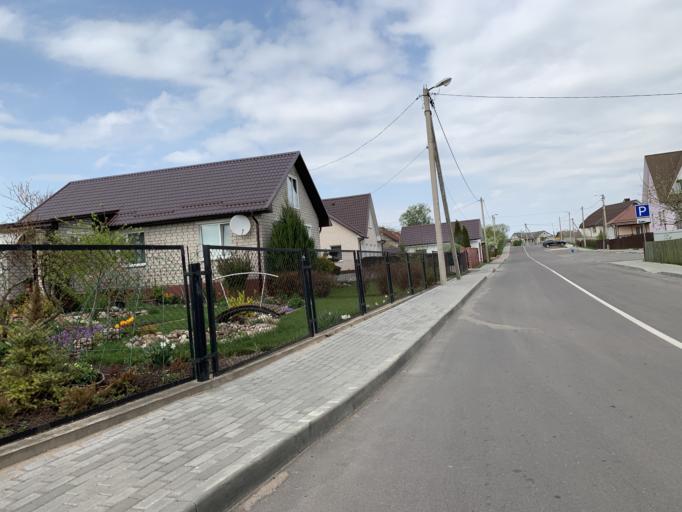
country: BY
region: Minsk
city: Nyasvizh
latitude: 53.2129
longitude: 26.6745
